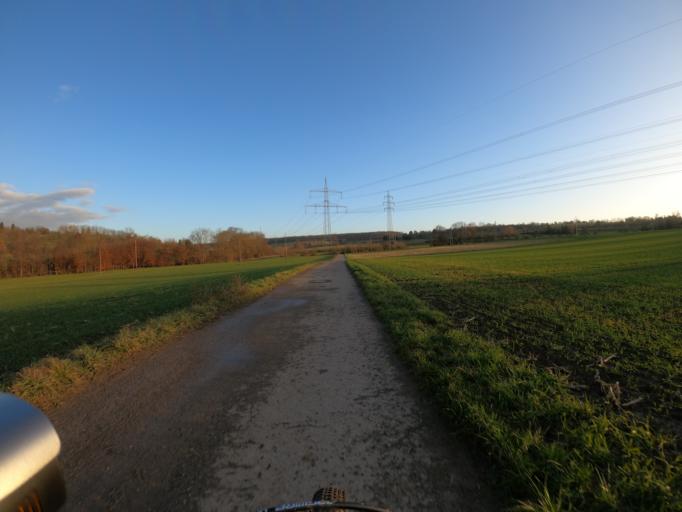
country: DE
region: Baden-Wuerttemberg
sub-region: Regierungsbezirk Stuttgart
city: Notzingen
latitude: 48.6729
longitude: 9.4342
